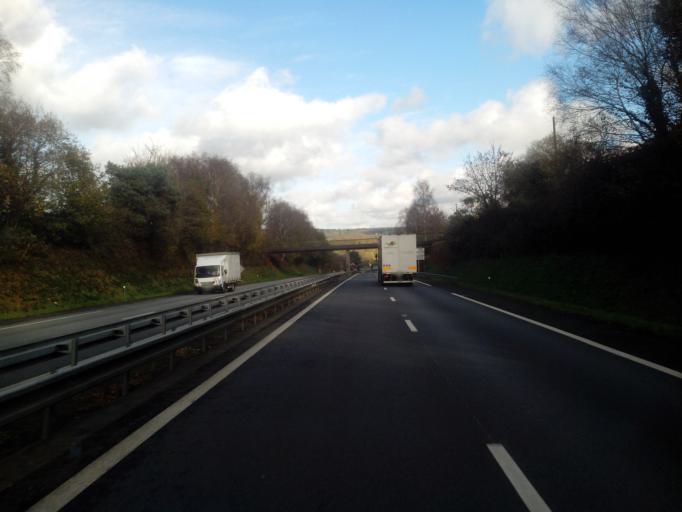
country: FR
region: Brittany
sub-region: Departement du Morbihan
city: Baud
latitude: 47.8665
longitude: -3.0719
